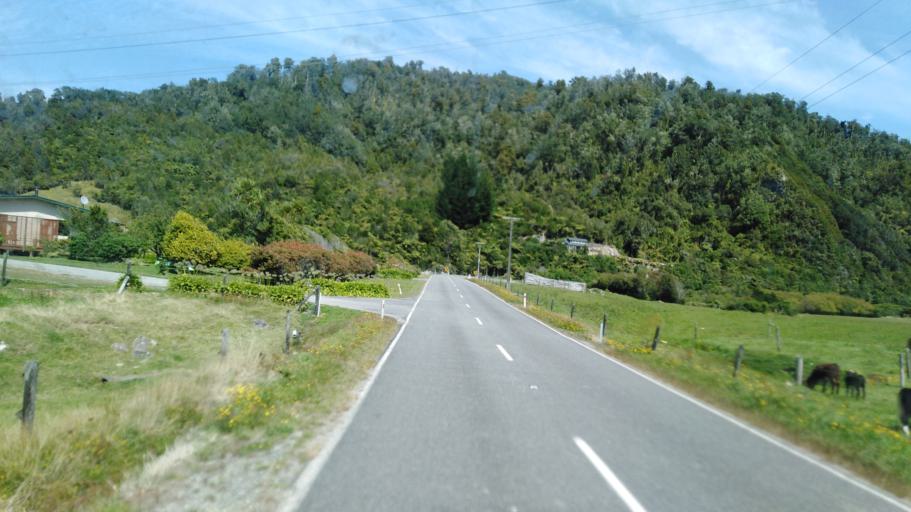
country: NZ
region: West Coast
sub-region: Buller District
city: Westport
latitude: -41.5330
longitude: 171.9617
